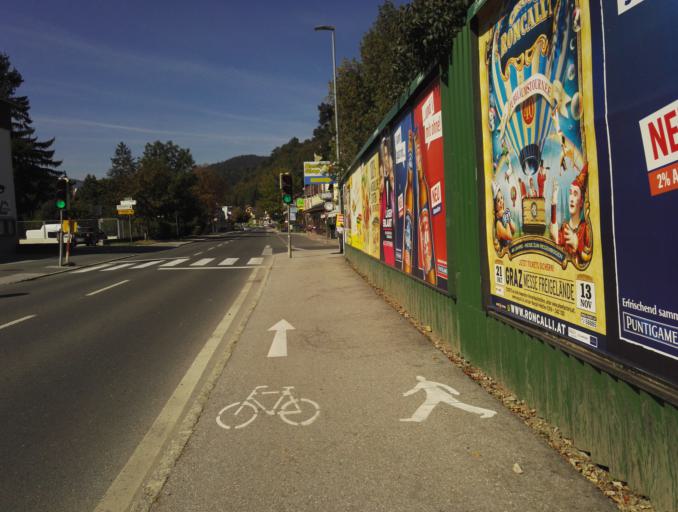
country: AT
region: Styria
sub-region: Politischer Bezirk Graz-Umgebung
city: Gratkorn
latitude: 47.1347
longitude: 15.3365
